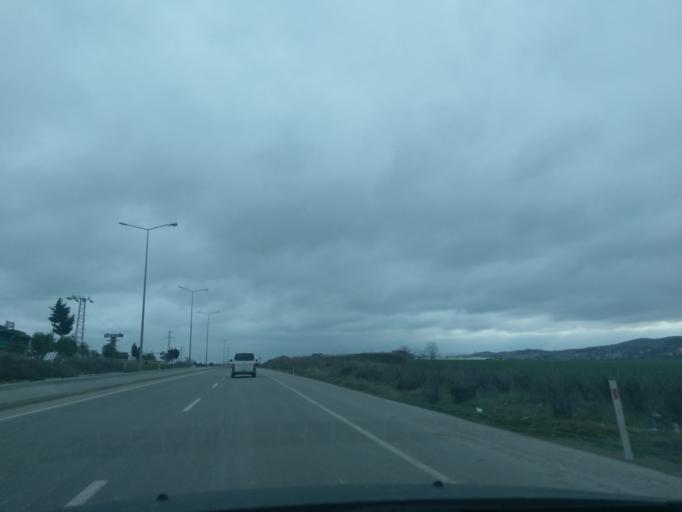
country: TR
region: Istanbul
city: Muratbey
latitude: 41.1186
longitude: 28.4955
